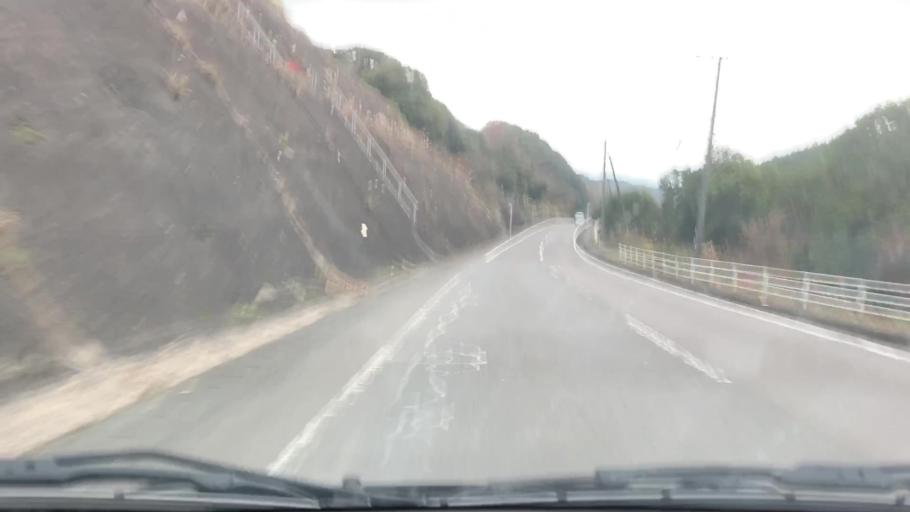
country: JP
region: Saga Prefecture
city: Ureshinomachi-shimojuku
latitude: 33.1143
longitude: 129.9761
